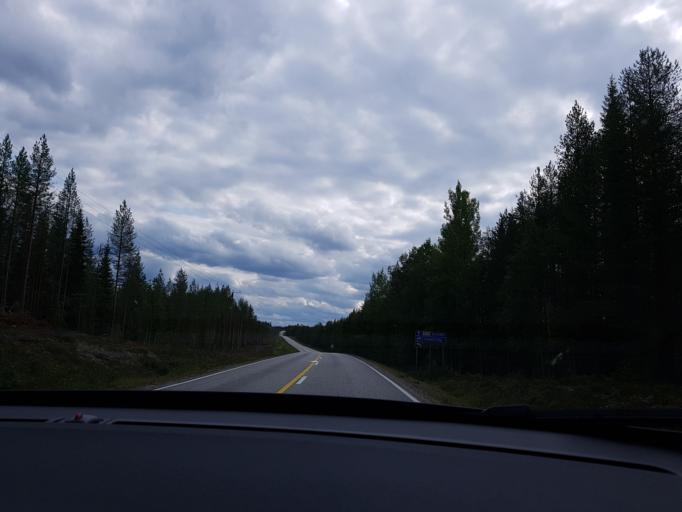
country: FI
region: Kainuu
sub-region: Kehys-Kainuu
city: Kuhmo
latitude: 64.3248
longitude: 29.8717
